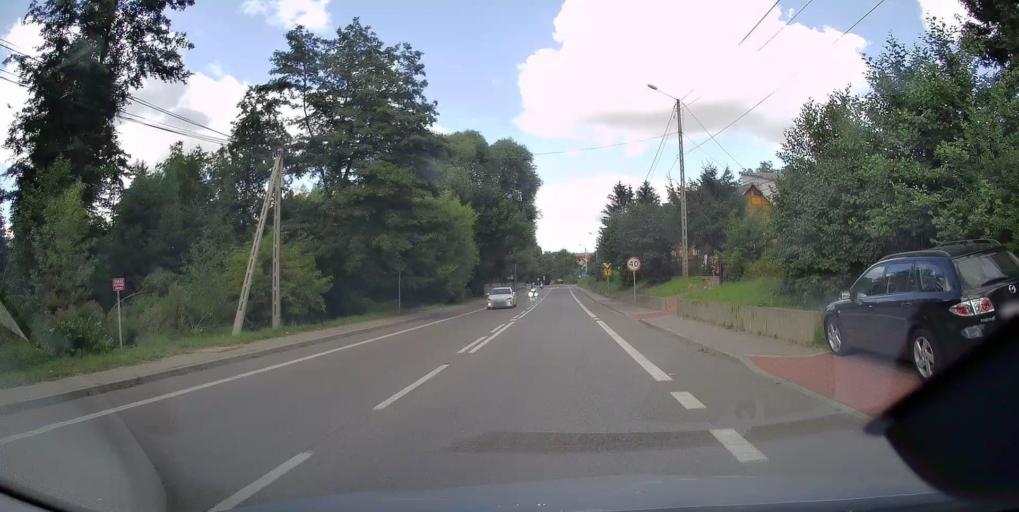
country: PL
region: Swietokrzyskie
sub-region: Powiat kielecki
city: Nowa Slupia
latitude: 50.8609
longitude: 21.0897
